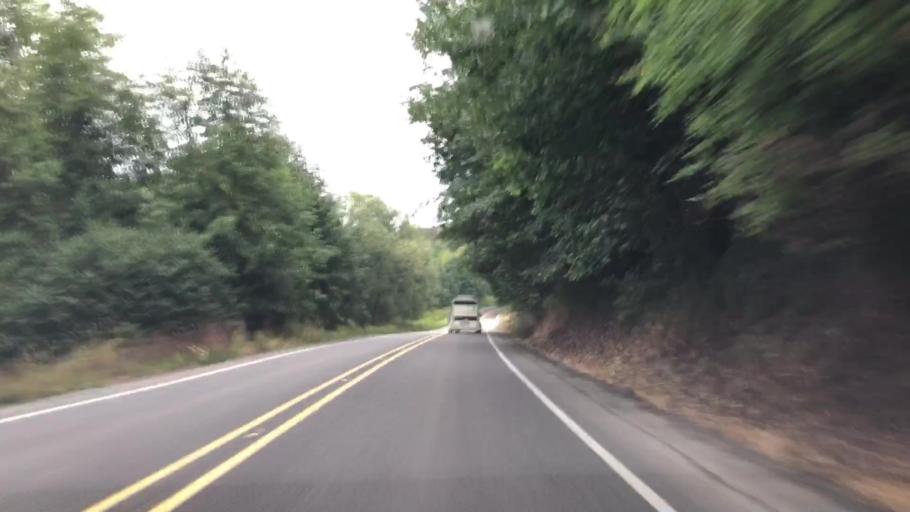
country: US
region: Washington
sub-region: Kitsap County
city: Navy Yard City
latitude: 47.5272
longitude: -122.7337
